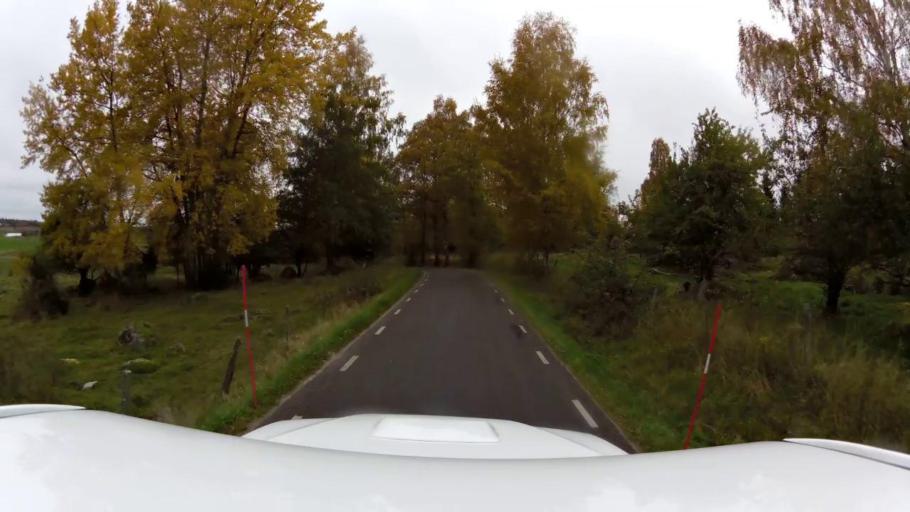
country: SE
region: OEstergoetland
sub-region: Linkopings Kommun
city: Linghem
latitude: 58.4828
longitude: 15.7921
